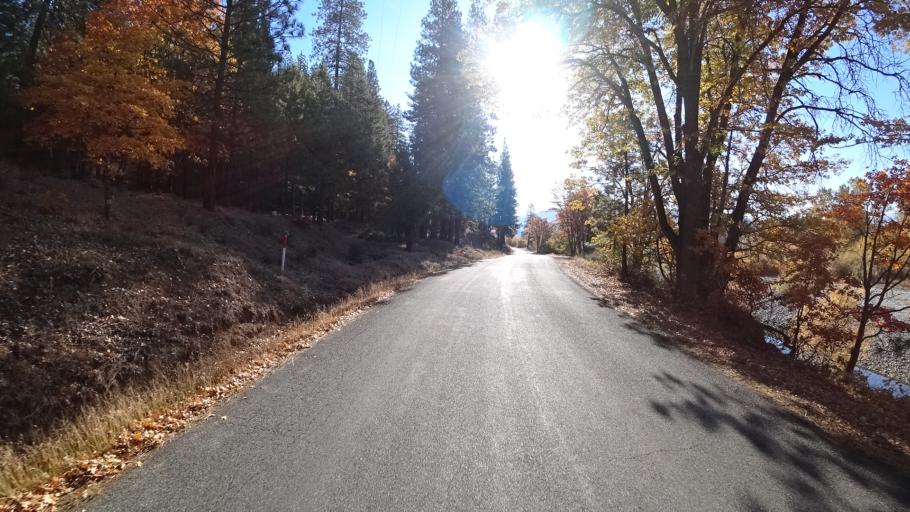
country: US
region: California
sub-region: Siskiyou County
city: Yreka
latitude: 41.6358
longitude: -122.9645
